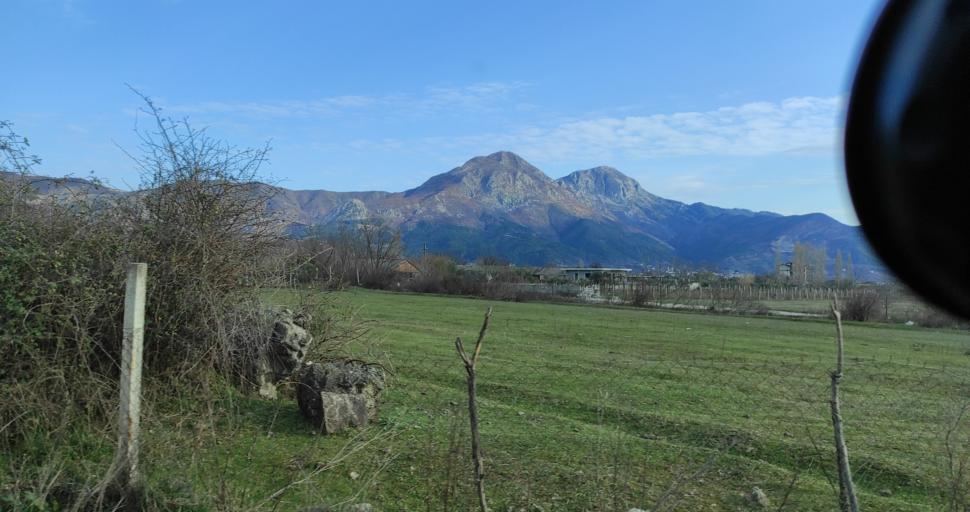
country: AL
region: Lezhe
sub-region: Rrethi i Lezhes
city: Kallmeti i Madh
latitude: 41.8784
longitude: 19.6743
